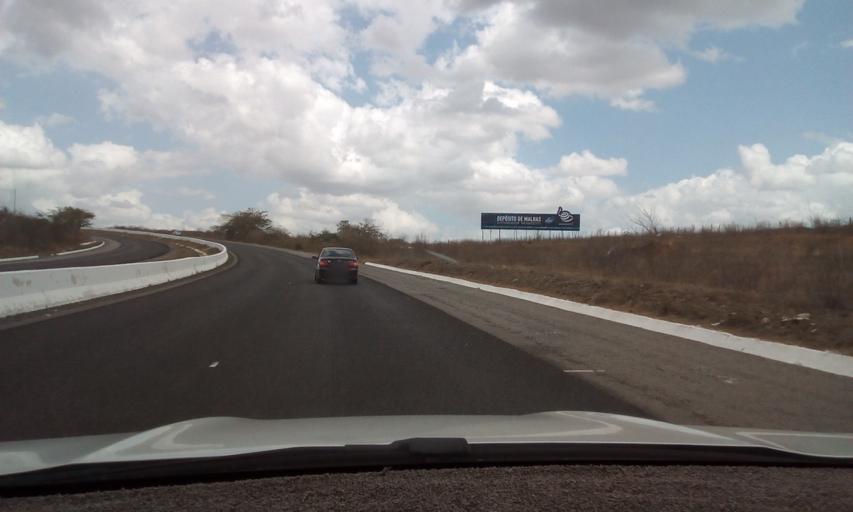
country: BR
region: Pernambuco
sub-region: Toritama
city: Toritama
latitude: -8.1137
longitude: -36.0152
